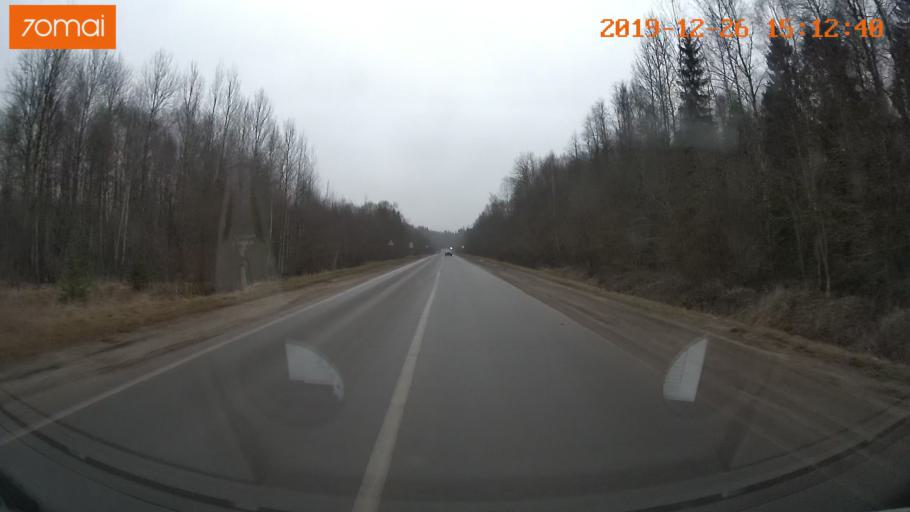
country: RU
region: Jaroslavl
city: Rybinsk
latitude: 58.1262
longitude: 38.8791
